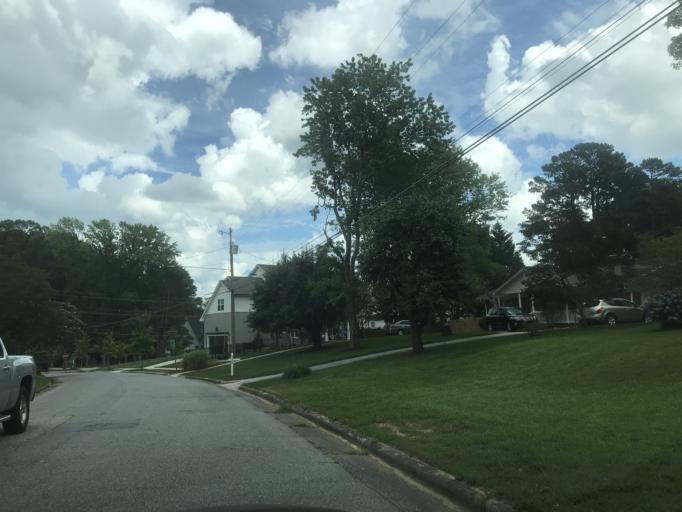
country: US
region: North Carolina
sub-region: Wake County
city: West Raleigh
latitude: 35.8410
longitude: -78.6367
